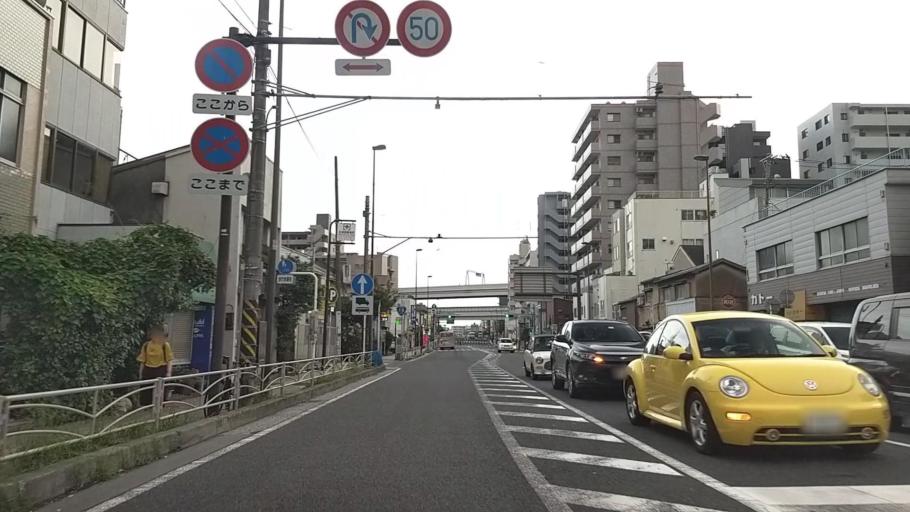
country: JP
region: Kanagawa
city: Yokohama
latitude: 35.4352
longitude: 139.6185
